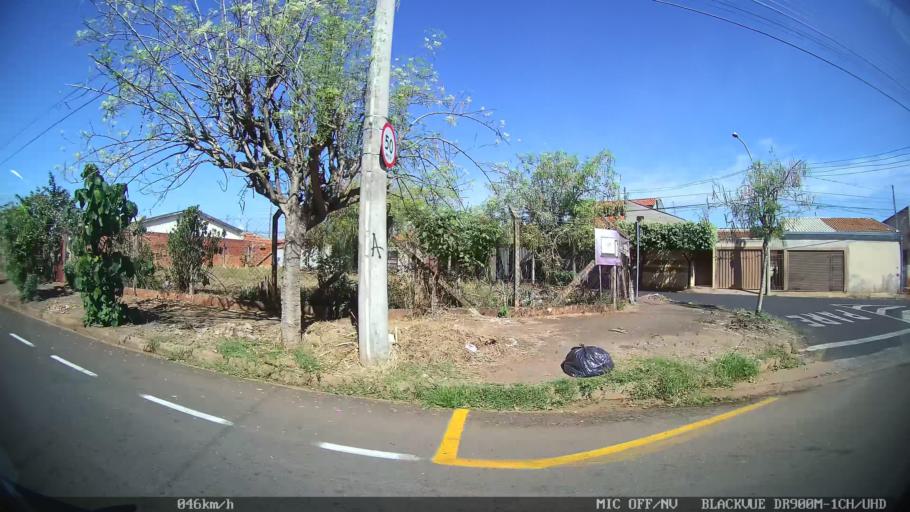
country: BR
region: Sao Paulo
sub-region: Sao Jose Do Rio Preto
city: Sao Jose do Rio Preto
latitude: -20.7654
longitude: -49.4020
